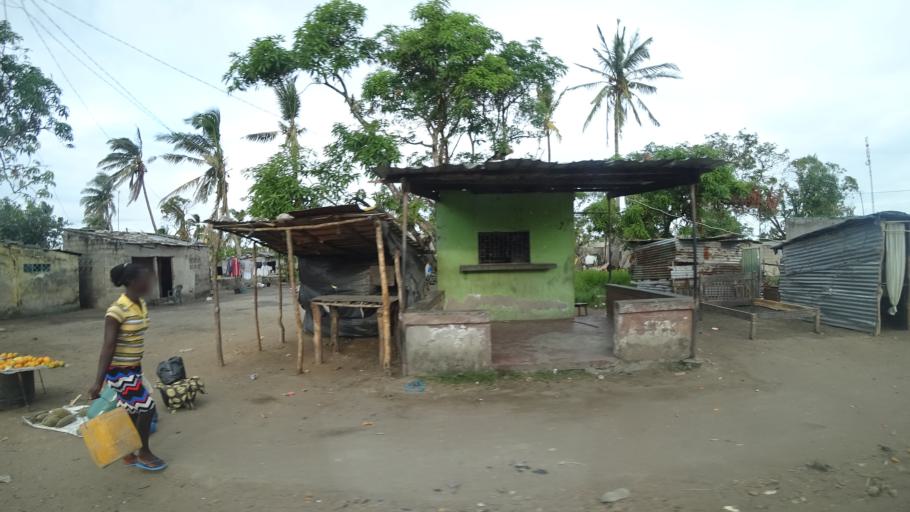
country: MZ
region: Sofala
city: Beira
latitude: -19.7744
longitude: 34.8846
